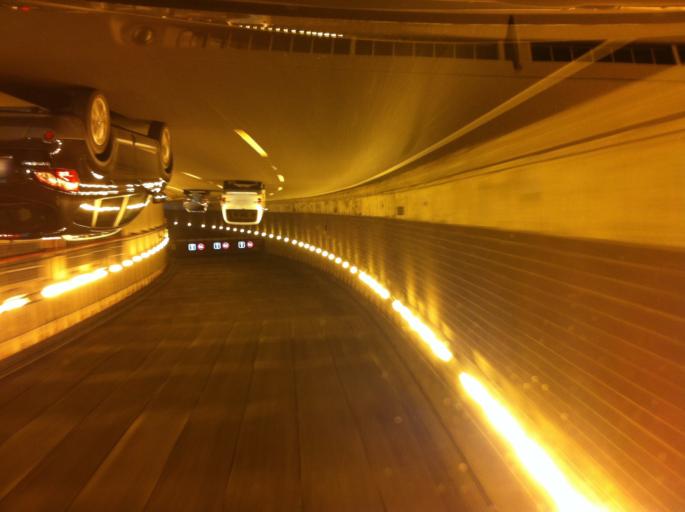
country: PT
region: Lisbon
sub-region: Odivelas
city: Pontinha
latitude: 38.7585
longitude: -9.2067
